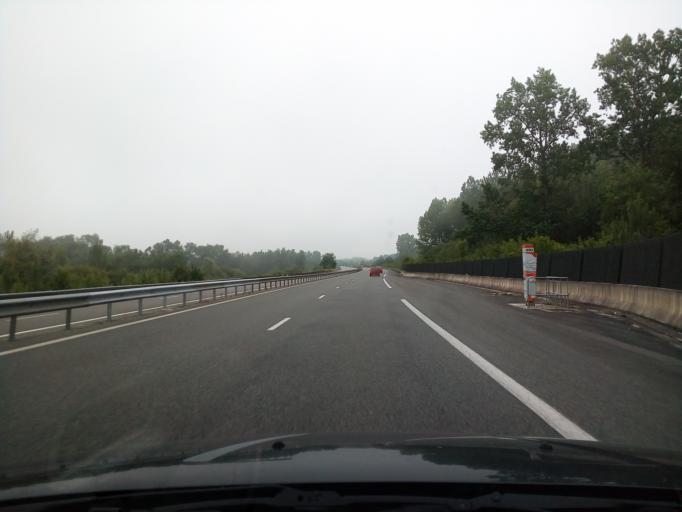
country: FR
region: Poitou-Charentes
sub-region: Departement de la Charente
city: Jarnac
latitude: 45.6754
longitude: -0.1555
